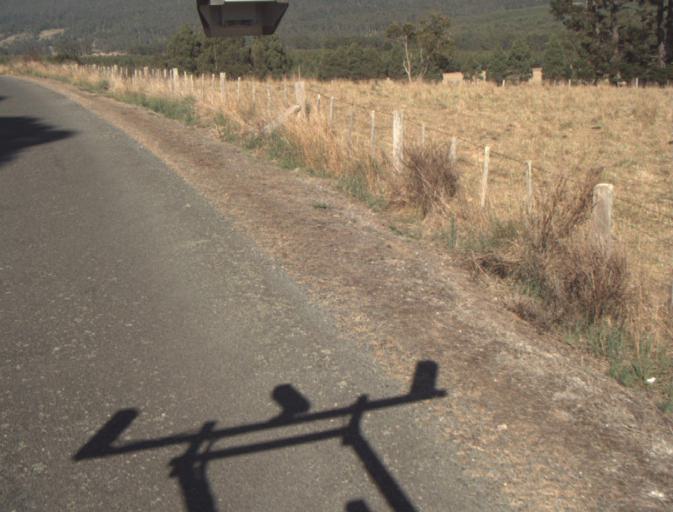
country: AU
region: Tasmania
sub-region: Launceston
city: Newstead
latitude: -41.3196
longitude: 147.3244
